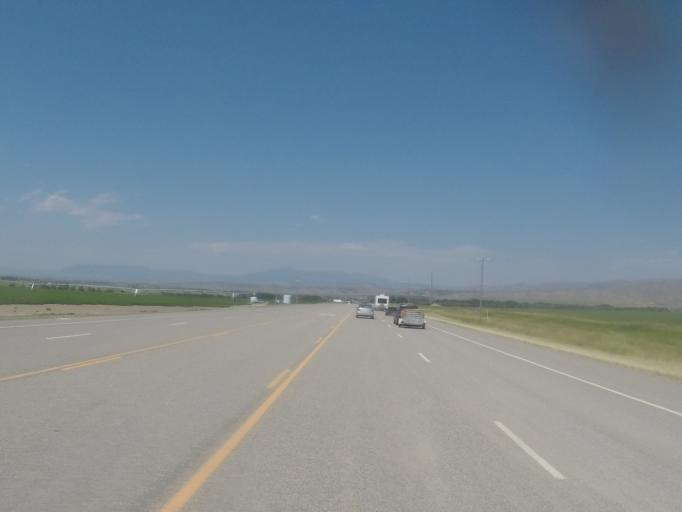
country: US
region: Montana
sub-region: Broadwater County
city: Townsend
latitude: 46.1438
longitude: -111.4744
